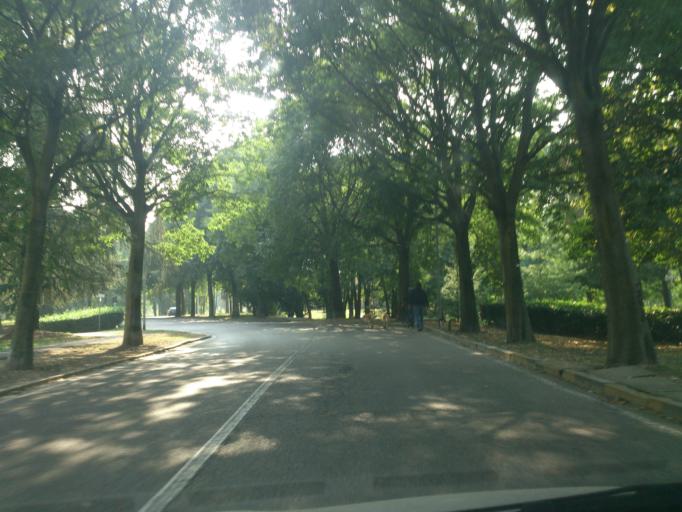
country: IT
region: Lombardy
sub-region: Citta metropolitana di Milano
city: San Donato Milanese
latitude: 45.4180
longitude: 9.2808
